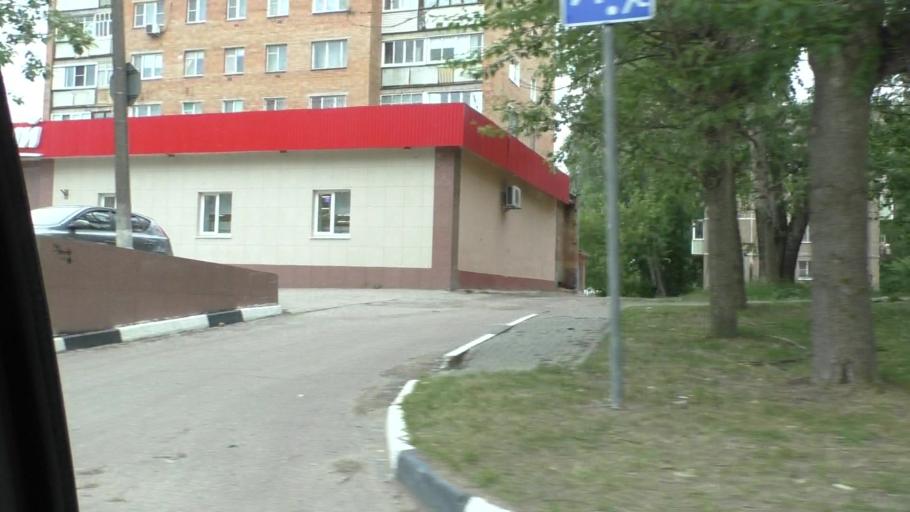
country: RU
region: Moskovskaya
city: Yegor'yevsk
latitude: 55.3663
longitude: 39.0576
